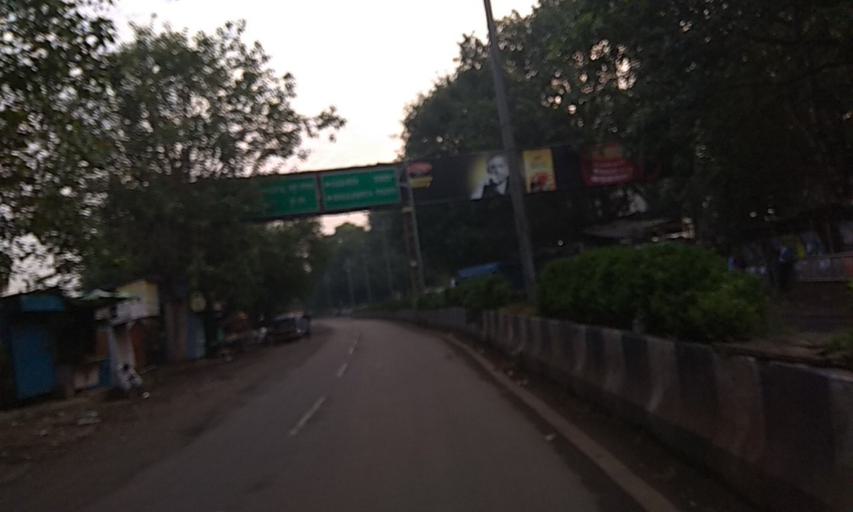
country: IN
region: Maharashtra
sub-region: Pune Division
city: Pune
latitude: 18.5217
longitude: 73.8555
